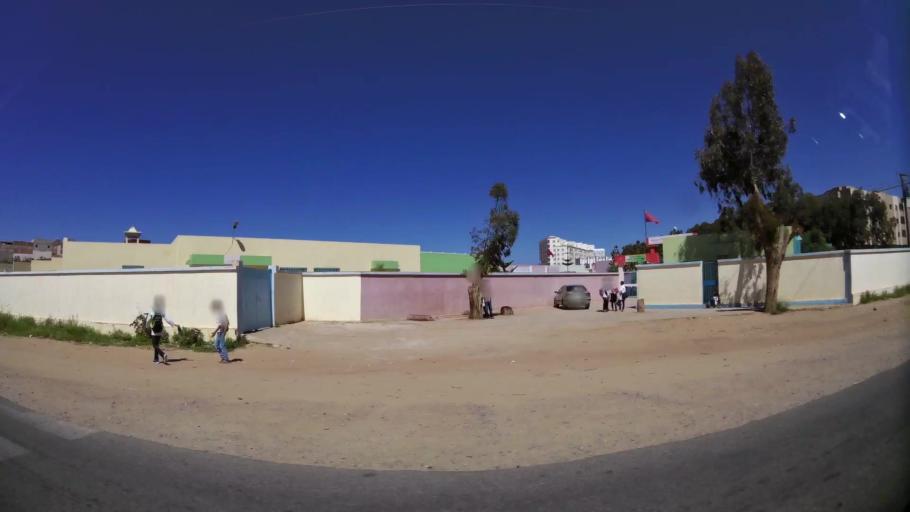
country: MA
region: Oriental
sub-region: Berkane-Taourirt
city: Madagh
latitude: 35.1252
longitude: -2.4226
